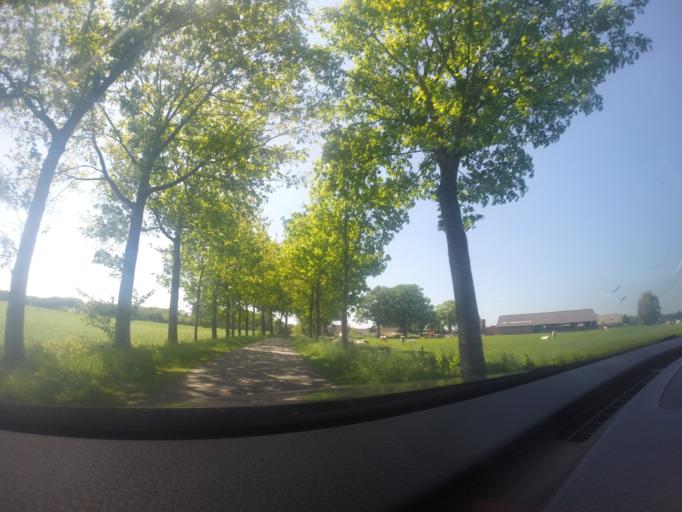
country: NL
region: Gelderland
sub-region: Gemeente Lochem
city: Almen
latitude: 52.1184
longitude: 6.2892
